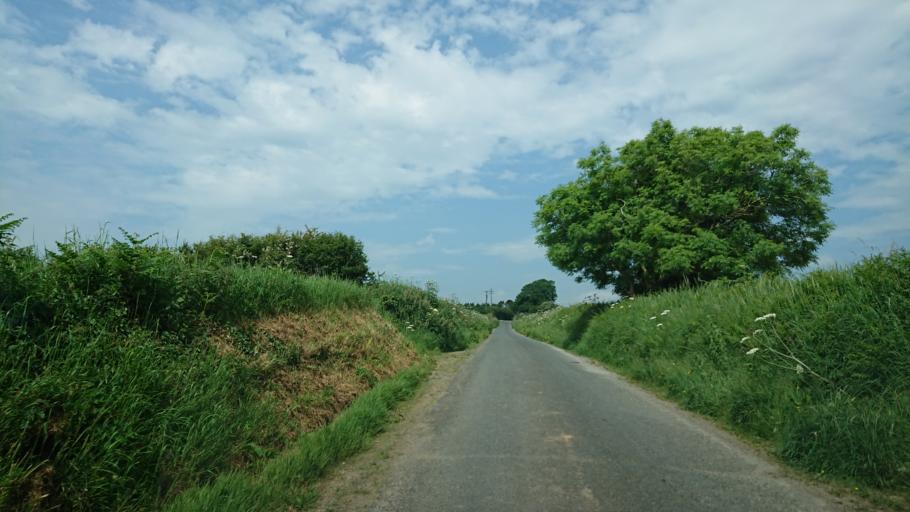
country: IE
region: Munster
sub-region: Waterford
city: Dunmore East
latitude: 52.2051
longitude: -6.9841
